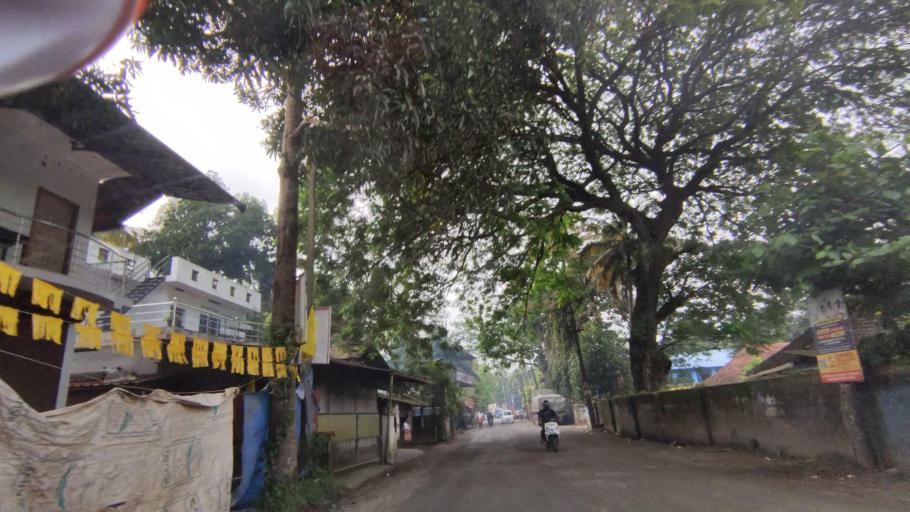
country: IN
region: Kerala
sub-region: Alappuzha
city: Shertallai
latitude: 9.6693
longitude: 76.4237
